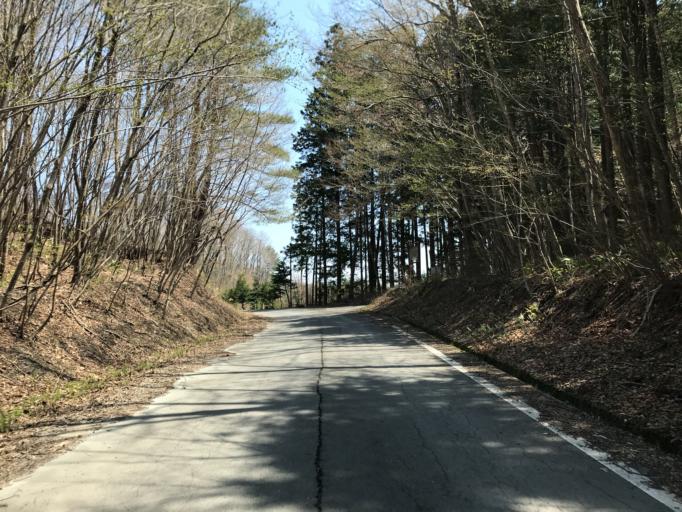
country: JP
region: Fukushima
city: Ishikawa
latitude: 36.9958
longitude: 140.5532
